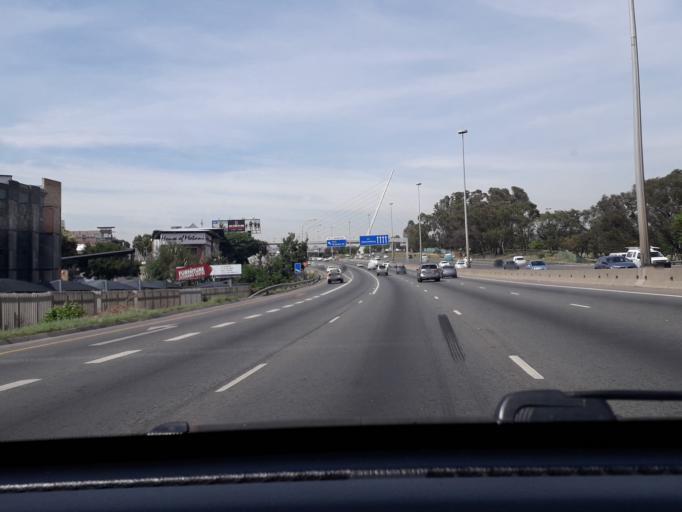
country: ZA
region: Gauteng
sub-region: City of Johannesburg Metropolitan Municipality
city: Modderfontein
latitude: -26.1027
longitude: 28.0785
